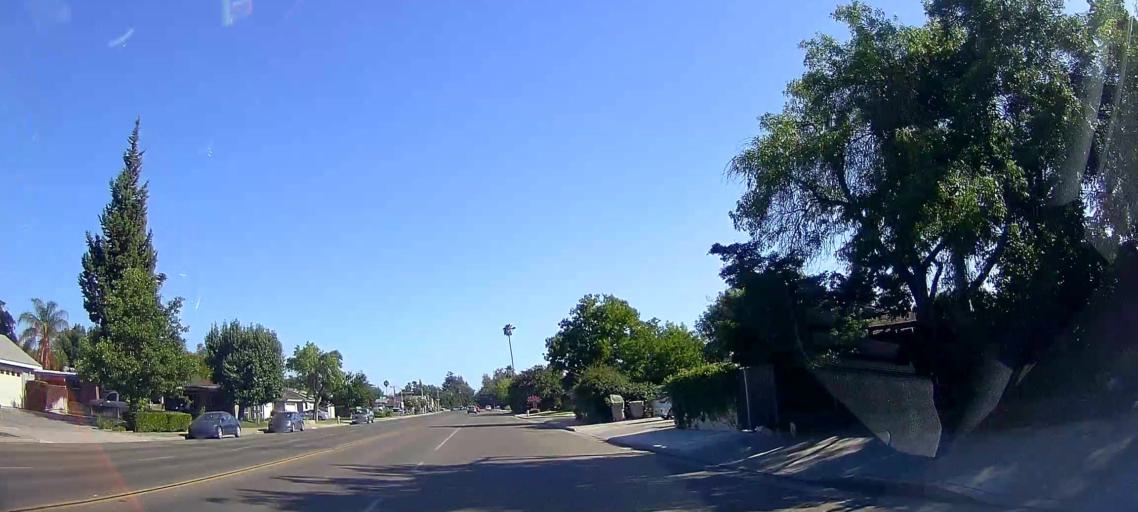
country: US
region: California
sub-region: Fresno County
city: Fresno
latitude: 36.8107
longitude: -119.7995
